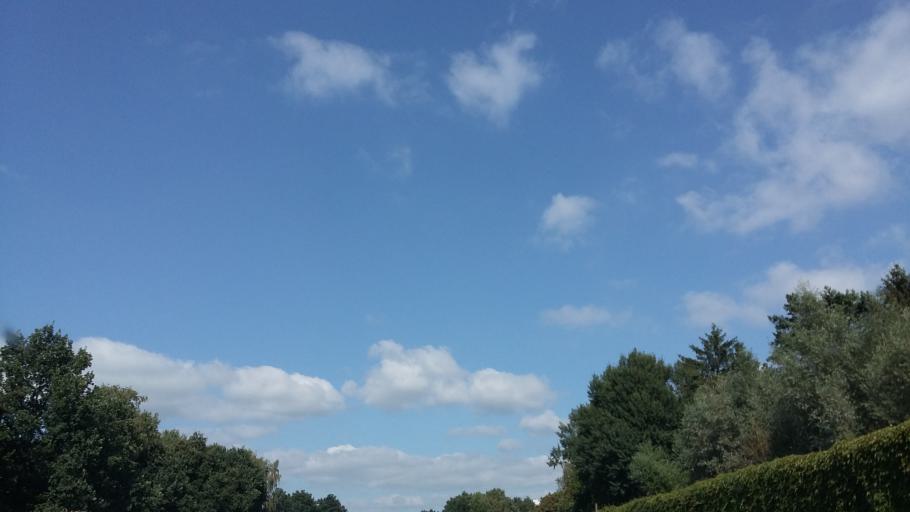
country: DE
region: Bremen
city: Bremen
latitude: 53.1099
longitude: 8.8066
